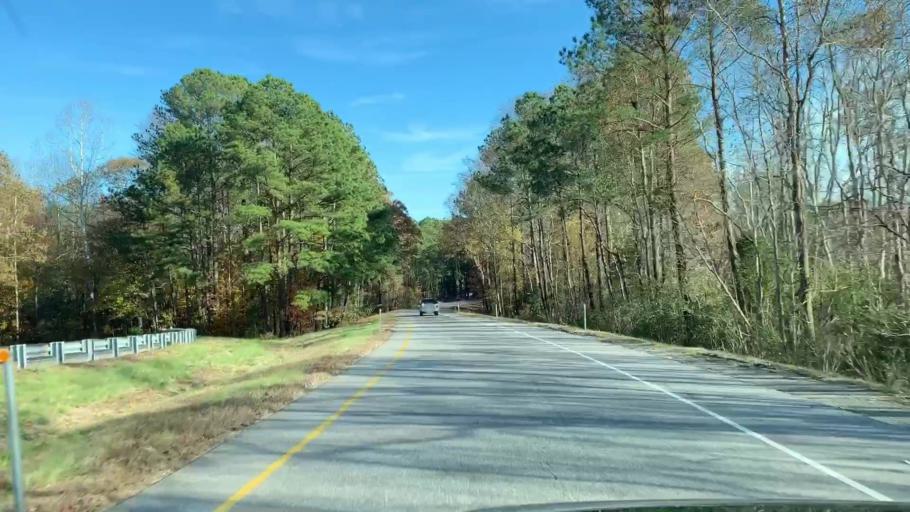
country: US
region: Virginia
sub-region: James City County
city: Williamsburg
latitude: 37.3831
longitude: -76.7631
